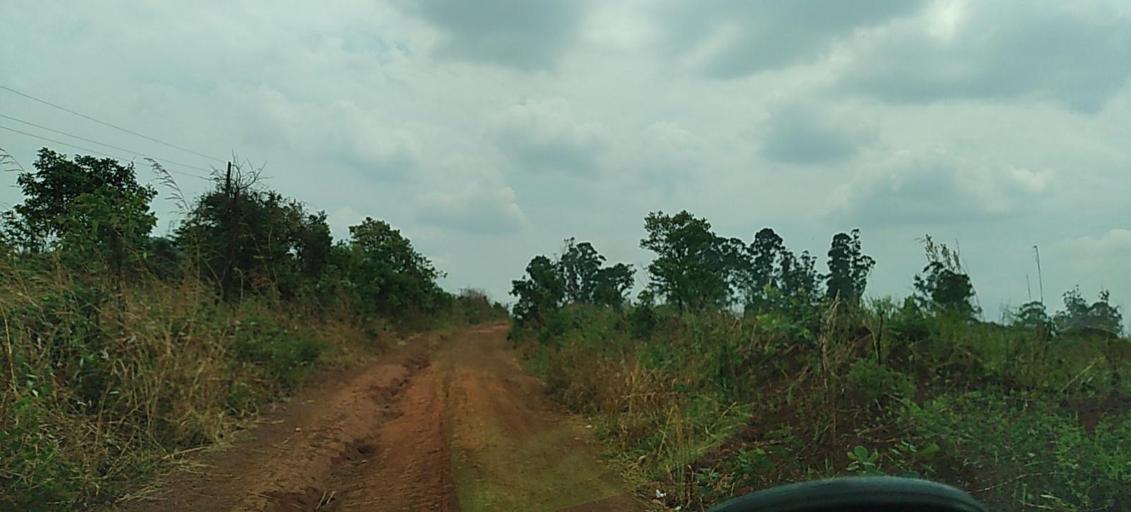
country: ZM
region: North-Western
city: Kansanshi
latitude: -12.0331
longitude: 26.4351
